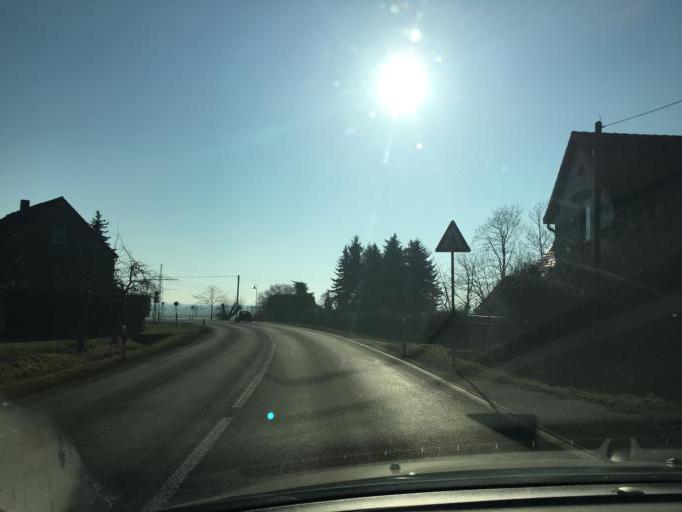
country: DE
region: Saxony
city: Grossposna
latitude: 51.2584
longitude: 12.5252
